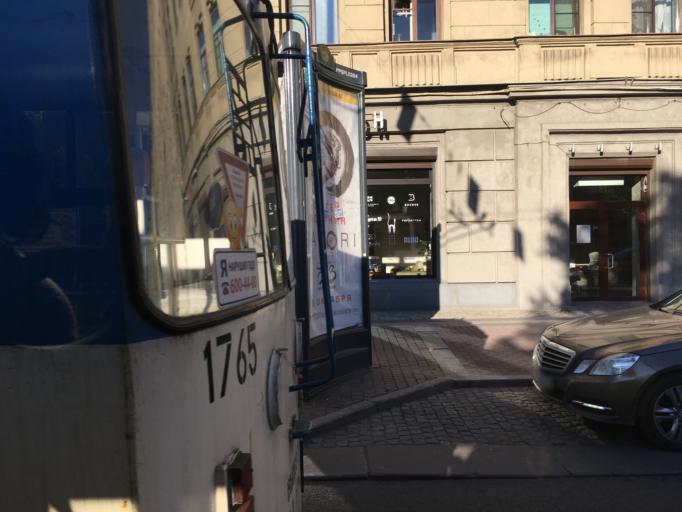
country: RU
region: St.-Petersburg
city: Admiralteisky
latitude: 59.8880
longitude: 30.3201
